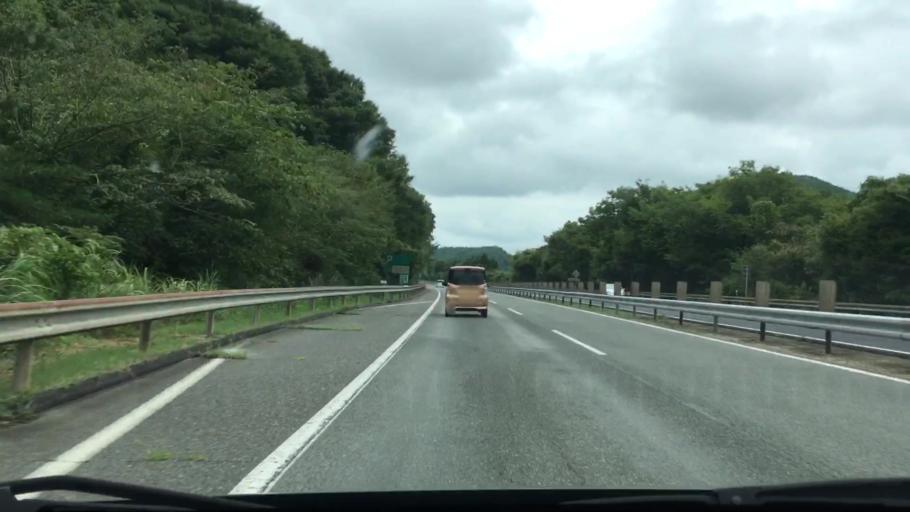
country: JP
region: Hiroshima
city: Miyoshi
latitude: 34.7666
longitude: 132.7963
